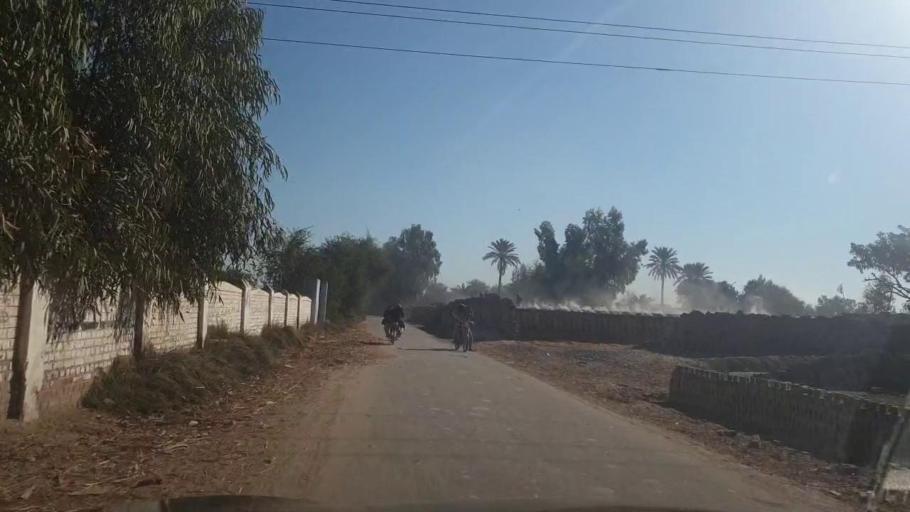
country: PK
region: Sindh
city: Ghotki
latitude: 27.9830
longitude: 69.3168
